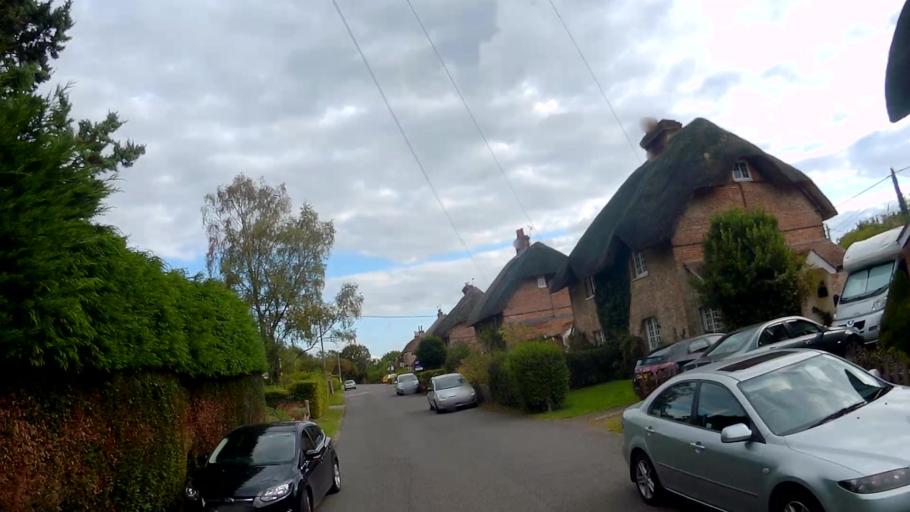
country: GB
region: England
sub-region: Hampshire
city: Overton
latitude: 51.1559
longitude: -1.2258
